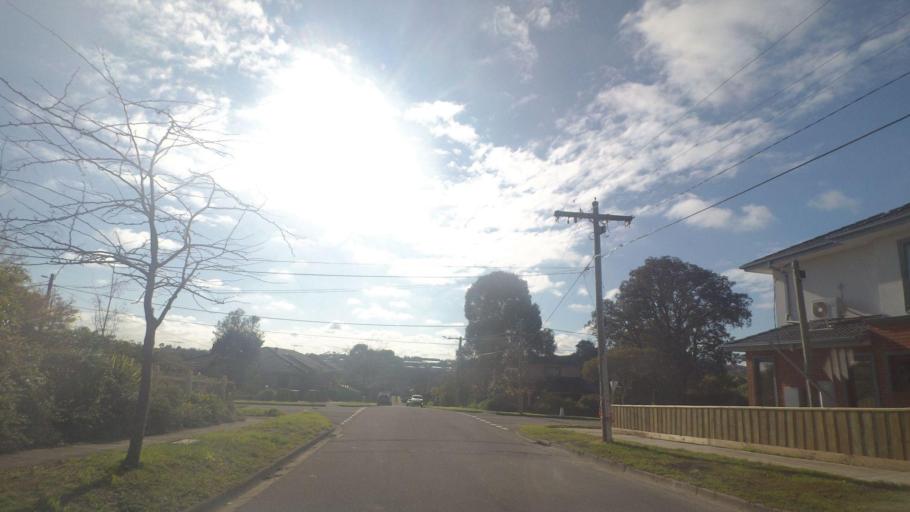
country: AU
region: Victoria
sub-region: Whitehorse
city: Mont Albert North
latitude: -37.7996
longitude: 145.1122
